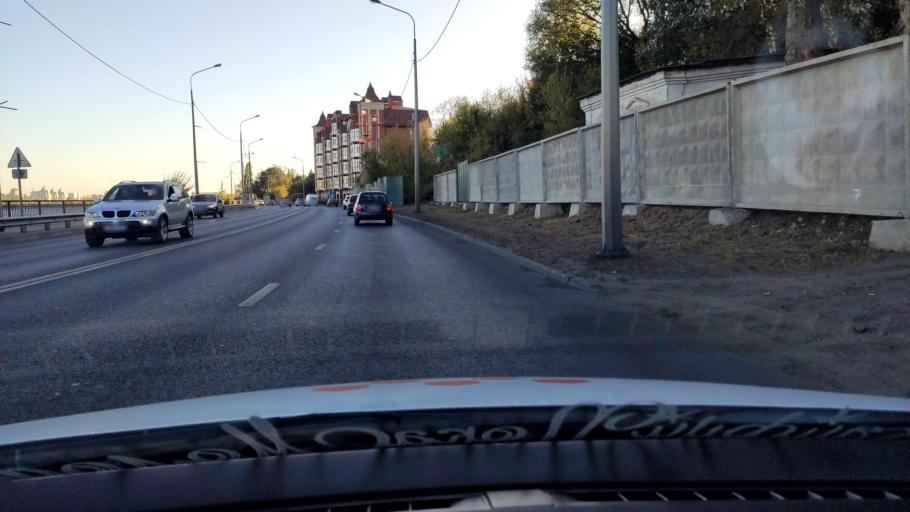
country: RU
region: Voronezj
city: Voronezh
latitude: 51.6840
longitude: 39.2284
